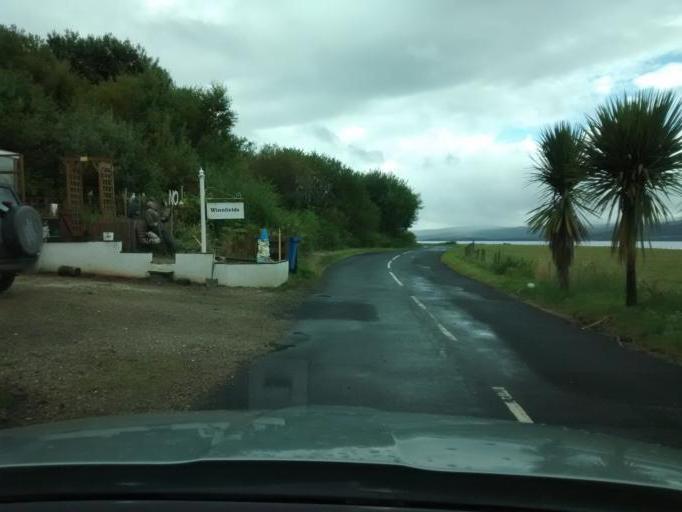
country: GB
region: Scotland
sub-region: North Ayrshire
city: Isle of Arran
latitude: 55.6296
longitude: -5.3908
